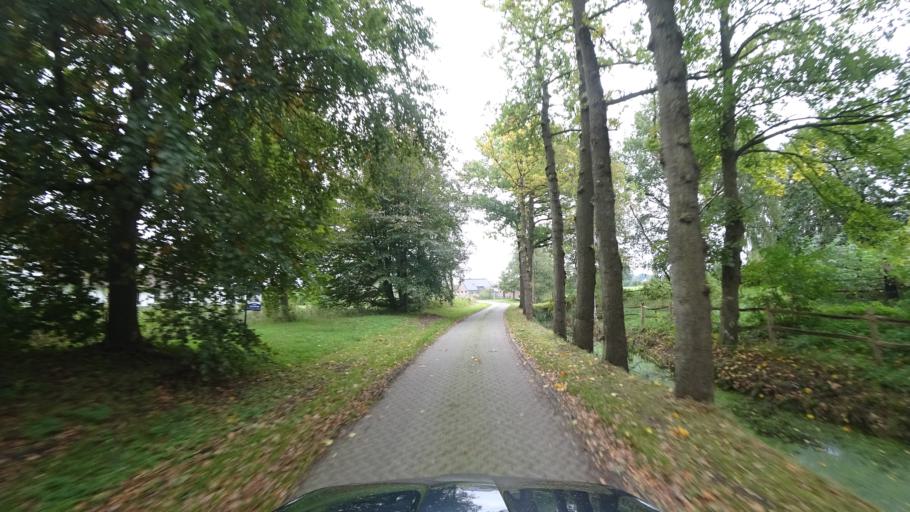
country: NL
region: Gelderland
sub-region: Gemeente Nijkerk
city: Nijkerk
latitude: 52.2458
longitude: 5.5125
